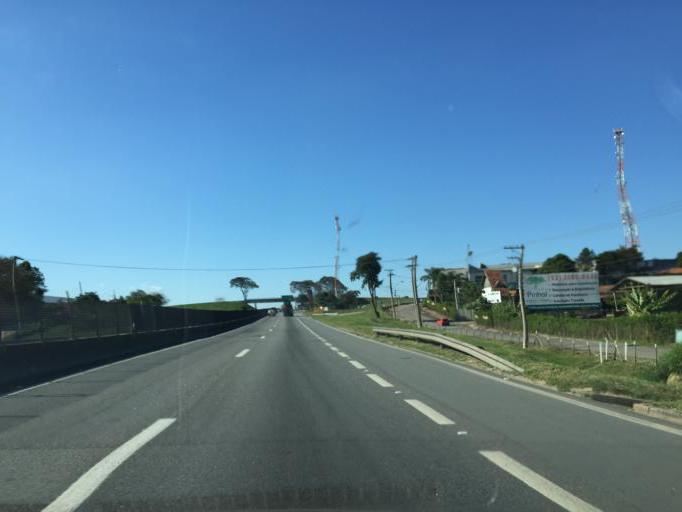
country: BR
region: Sao Paulo
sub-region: Lorena
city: Lorena
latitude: -22.7444
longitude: -45.0960
